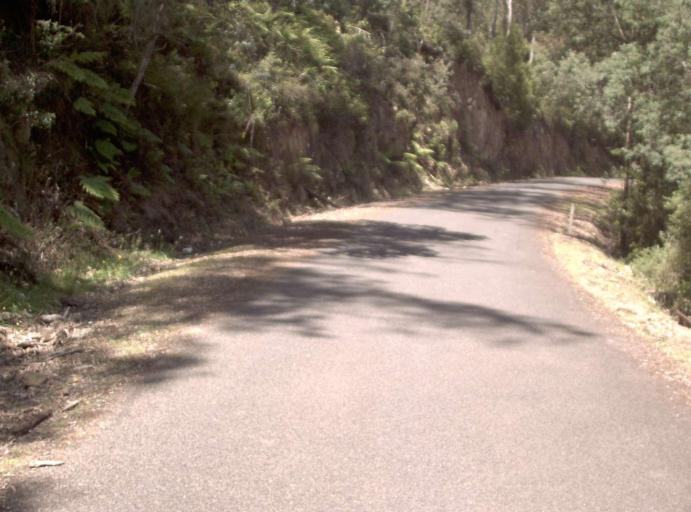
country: AU
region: New South Wales
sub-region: Bombala
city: Bombala
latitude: -37.4407
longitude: 148.9541
